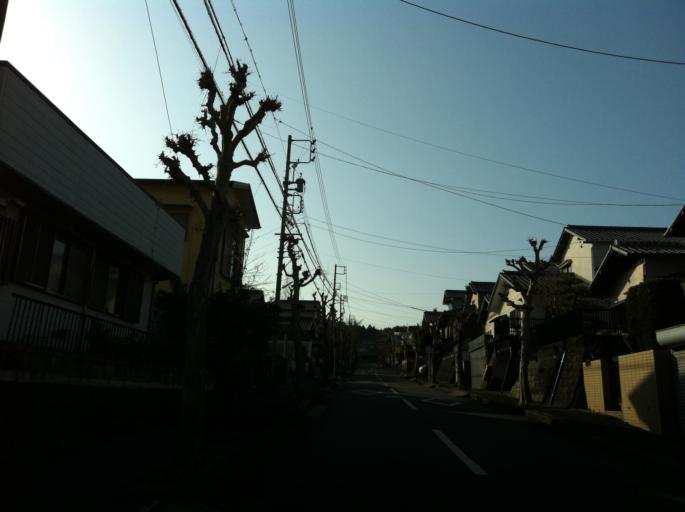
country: JP
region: Shizuoka
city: Shizuoka-shi
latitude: 34.9923
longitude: 138.4534
